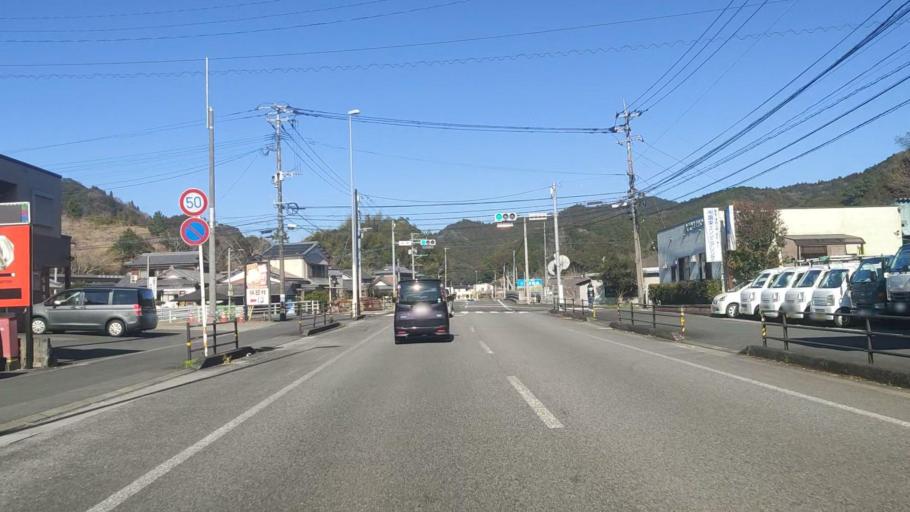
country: JP
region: Oita
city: Saiki
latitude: 32.9678
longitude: 131.8624
